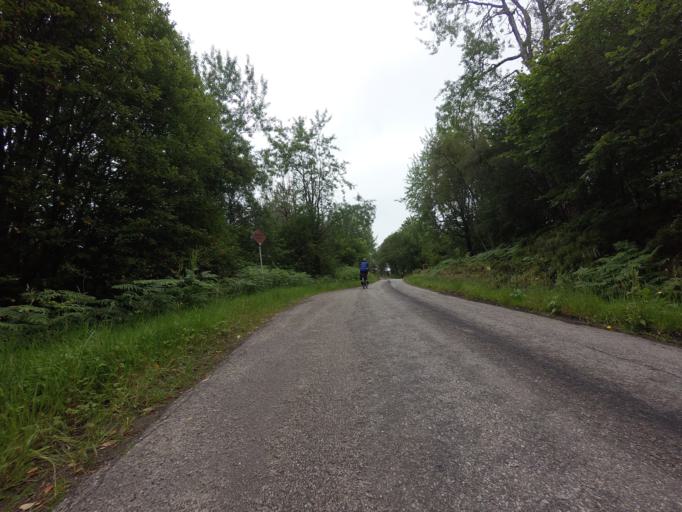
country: GB
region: Scotland
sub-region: Highland
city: Evanton
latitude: 57.9620
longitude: -4.4080
